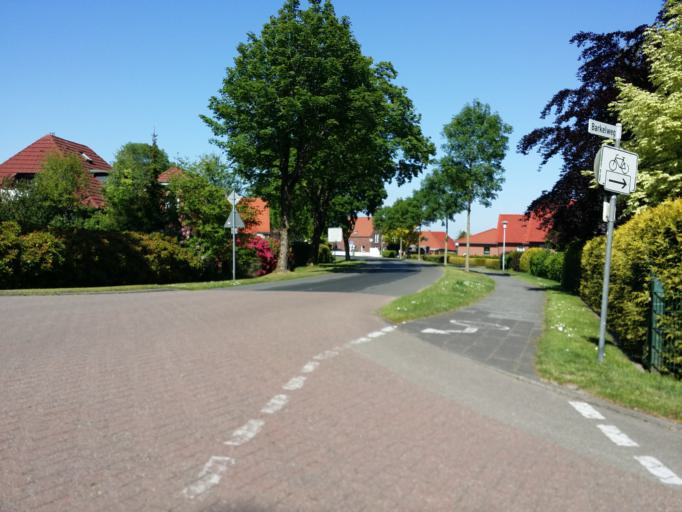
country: DE
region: Lower Saxony
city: Esens
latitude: 53.6477
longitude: 7.6183
